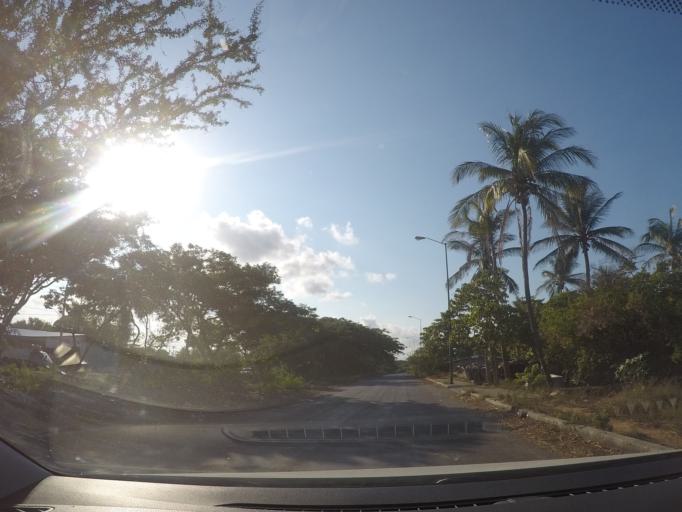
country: MX
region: Oaxaca
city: Juchitan de Zaragoza
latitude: 16.4256
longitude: -95.0307
